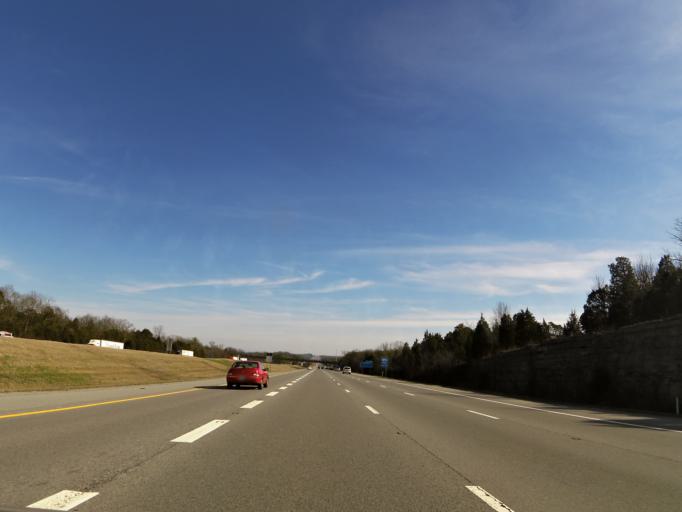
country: US
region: Tennessee
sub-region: Rutherford County
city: Smyrna
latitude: 35.9559
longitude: -86.5559
